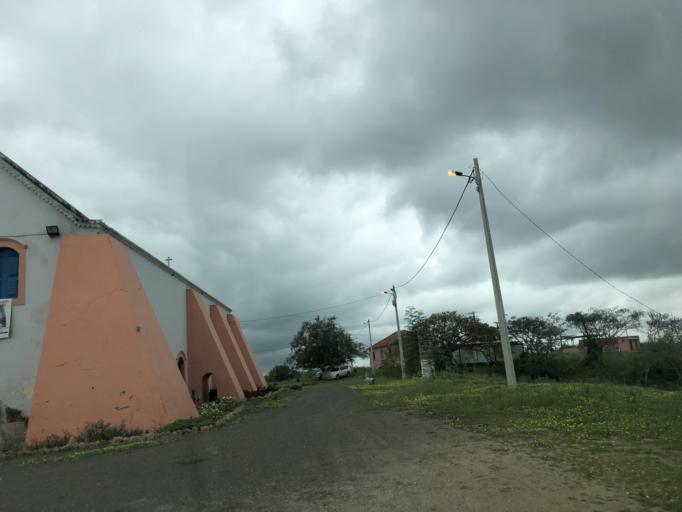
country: AO
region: Cuanza Norte
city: N'dalatando
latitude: -9.6277
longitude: 14.2553
